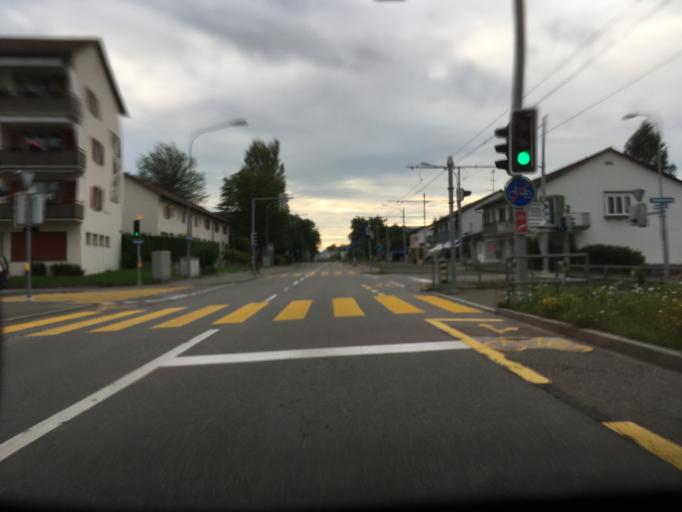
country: CH
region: Zurich
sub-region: Bezirk Zuerich
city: Zuerich (Kreis 12) / Hirzenbach
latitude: 47.3983
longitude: 8.5918
